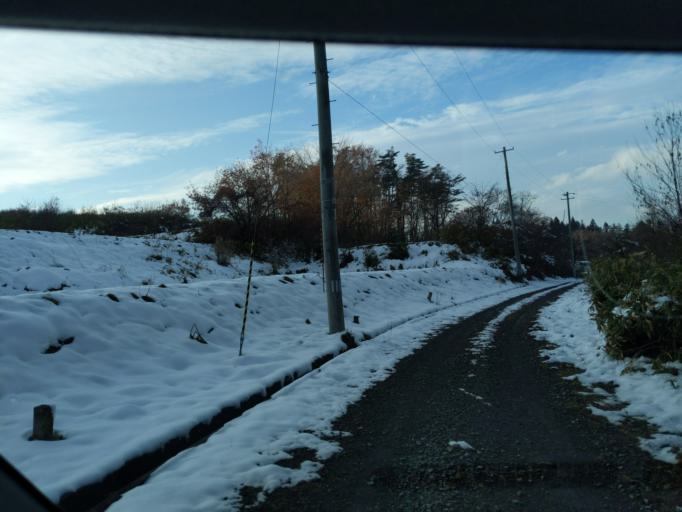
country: JP
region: Iwate
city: Mizusawa
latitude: 39.0382
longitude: 141.1027
